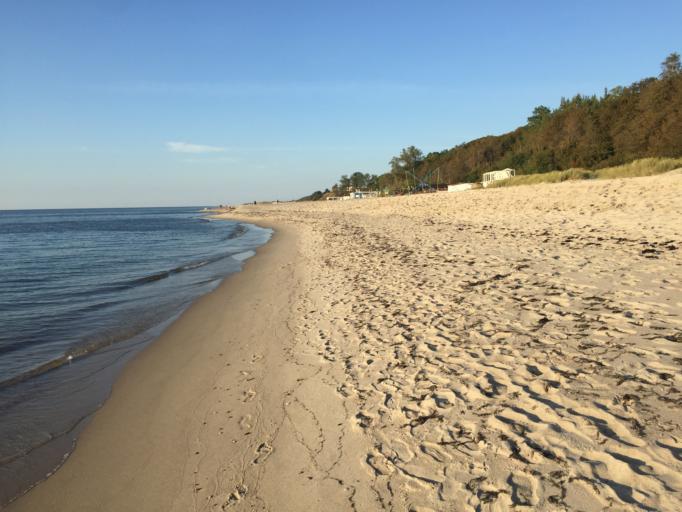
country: RU
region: Kaliningrad
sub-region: Gorod Kaliningrad
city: Yantarnyy
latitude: 54.8653
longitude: 19.9324
